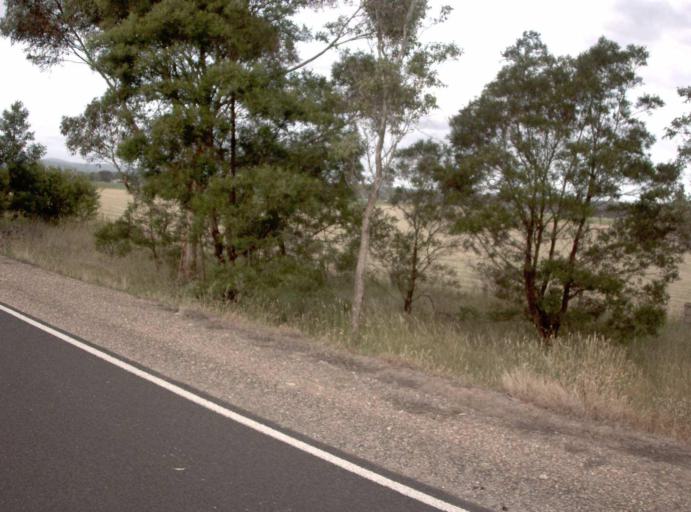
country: AU
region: Victoria
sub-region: Wellington
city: Sale
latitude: -37.8507
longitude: 147.0539
